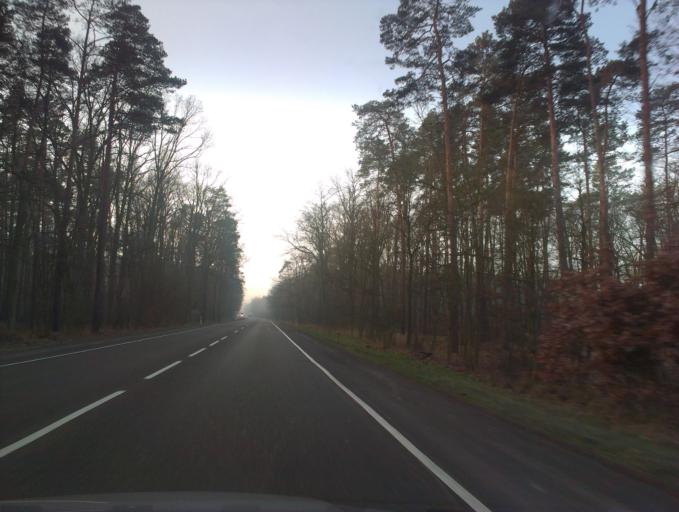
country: PL
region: Greater Poland Voivodeship
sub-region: Powiat obornicki
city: Rogozno
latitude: 52.7176
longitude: 16.9113
